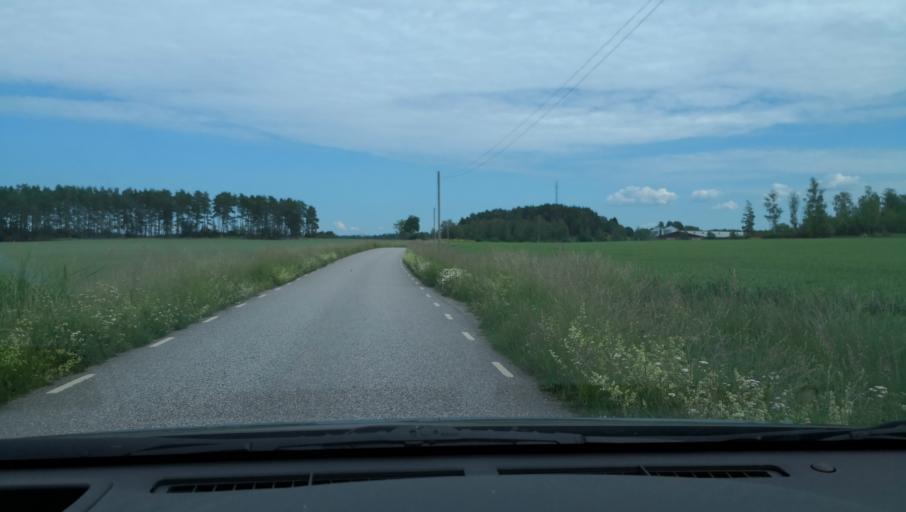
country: SE
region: Uppsala
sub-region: Enkopings Kommun
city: Orsundsbro
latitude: 59.6938
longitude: 17.3944
